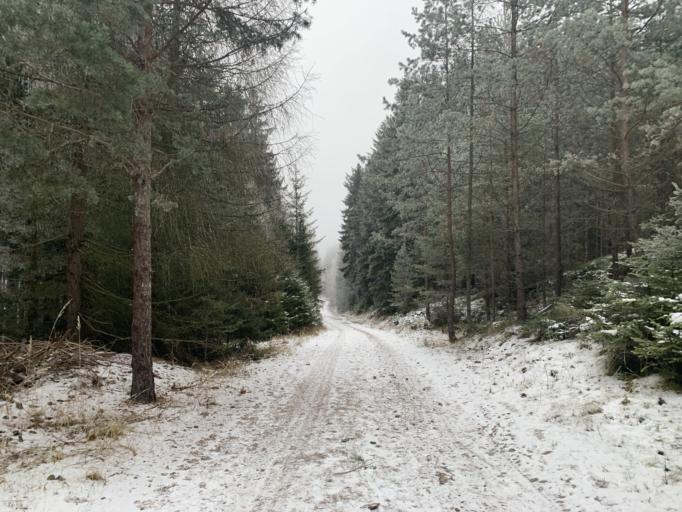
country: CZ
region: Central Bohemia
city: Rozmital pod Tremsinem
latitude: 49.5779
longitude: 13.8286
